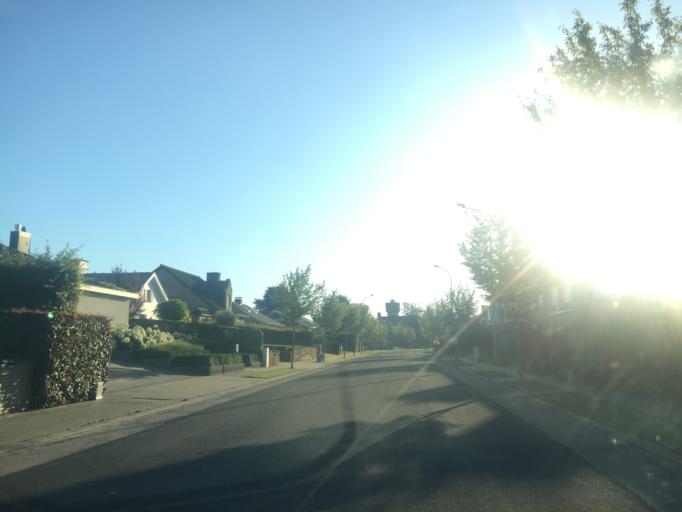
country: BE
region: Flanders
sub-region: Provincie West-Vlaanderen
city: Izegem
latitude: 50.9101
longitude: 3.2243
